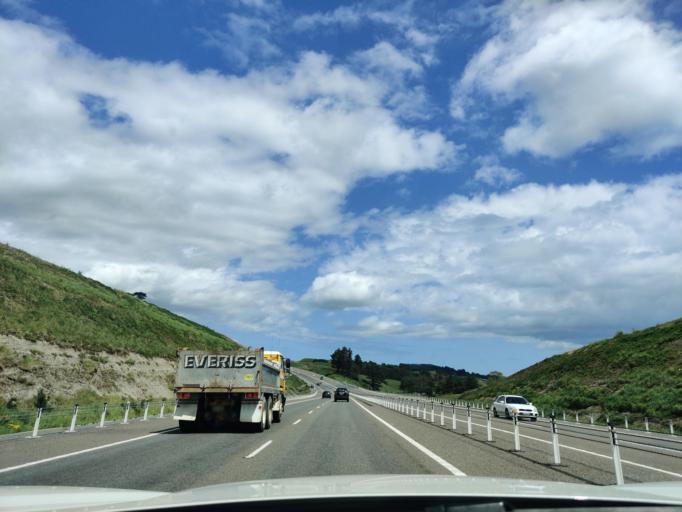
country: NZ
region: Wellington
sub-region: Porirua City
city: Porirua
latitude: -41.0639
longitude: 174.9444
